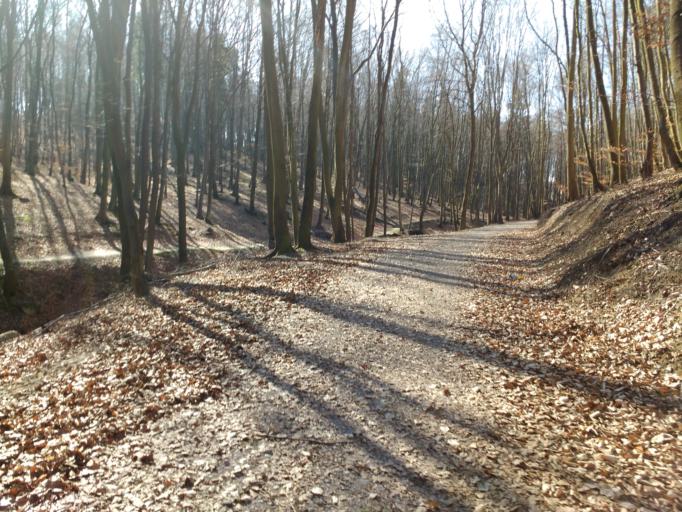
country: PL
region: Pomeranian Voivodeship
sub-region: Gdynia
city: Wielki Kack
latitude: 54.4807
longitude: 18.5151
